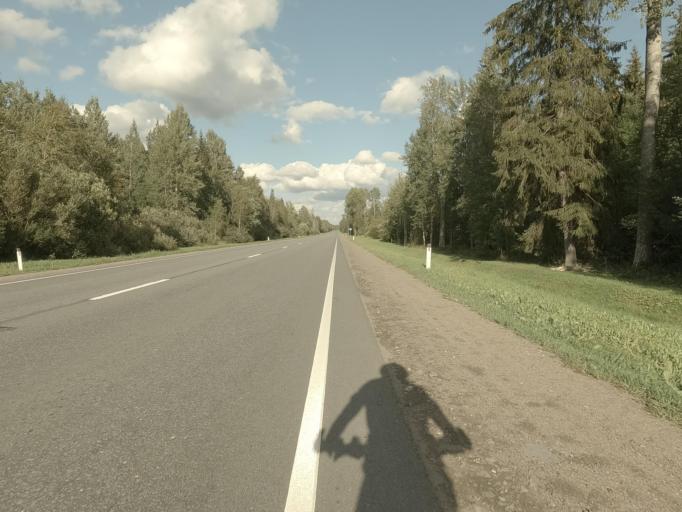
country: RU
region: Leningrad
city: Nikol'skoye
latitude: 59.6734
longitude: 30.9154
